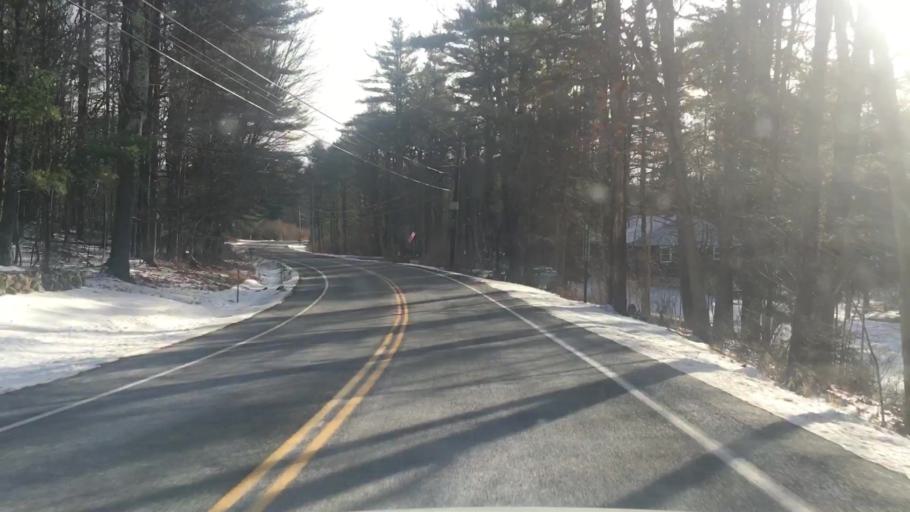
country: US
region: New Hampshire
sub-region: Merrimack County
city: Canterbury
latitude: 43.2968
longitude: -71.5635
